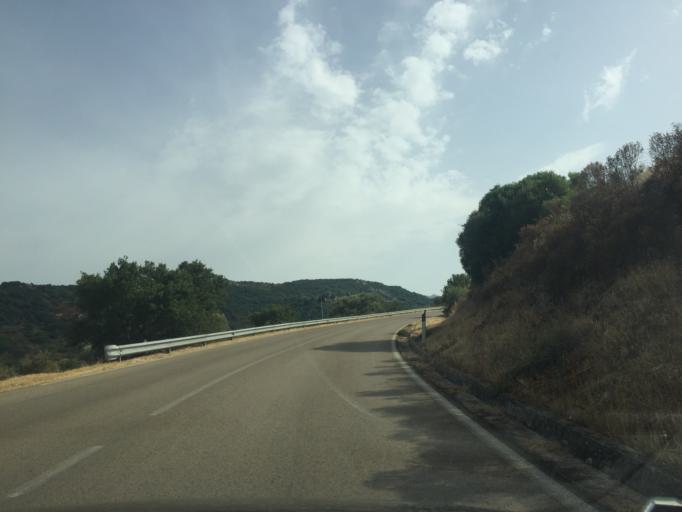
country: IT
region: Sardinia
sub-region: Provincia di Olbia-Tempio
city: Luras
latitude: 40.9554
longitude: 9.2069
